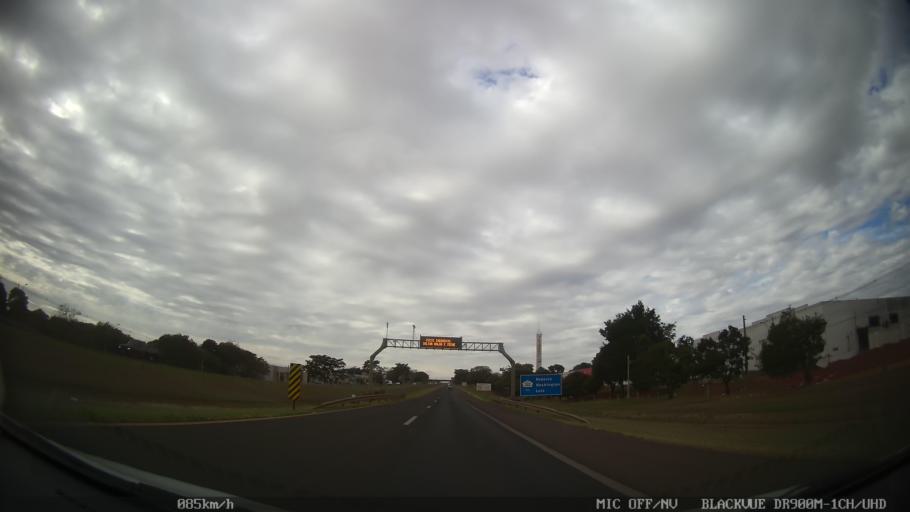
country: BR
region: Sao Paulo
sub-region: Bady Bassitt
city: Bady Bassitt
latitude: -20.8068
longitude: -49.5140
